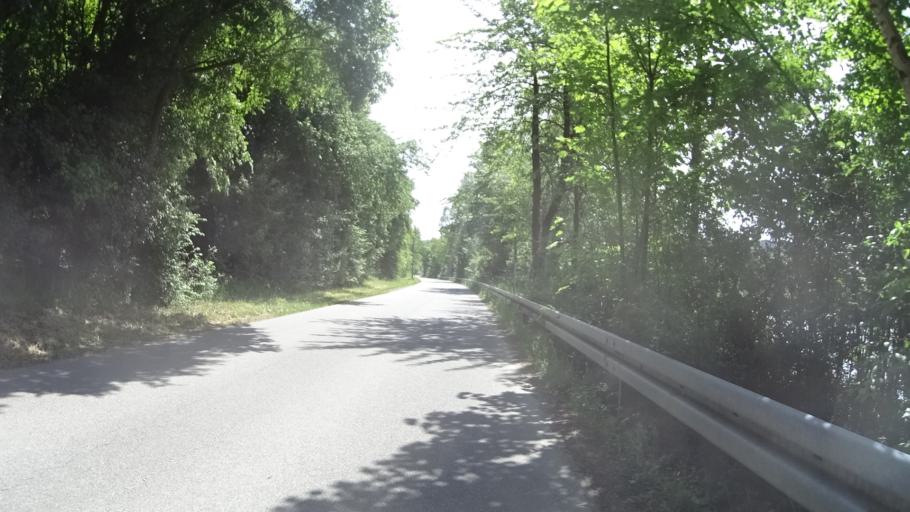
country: DE
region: Bavaria
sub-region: Lower Bavaria
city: Teugn
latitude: 48.9302
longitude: 12.0042
